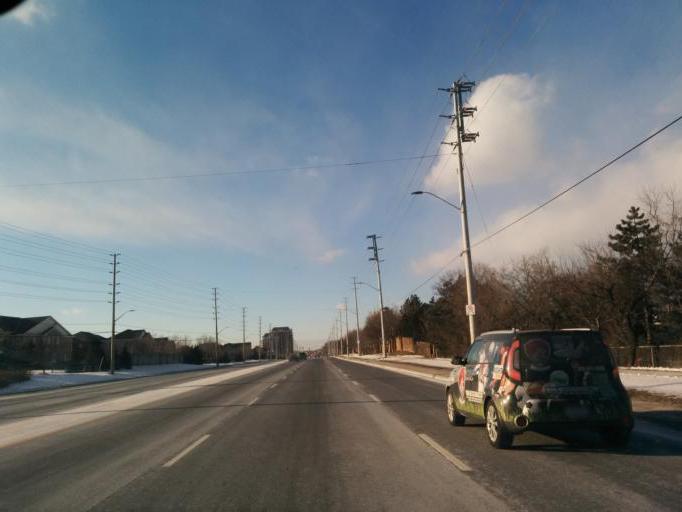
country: CA
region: Ontario
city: Mississauga
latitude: 43.5879
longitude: -79.6631
